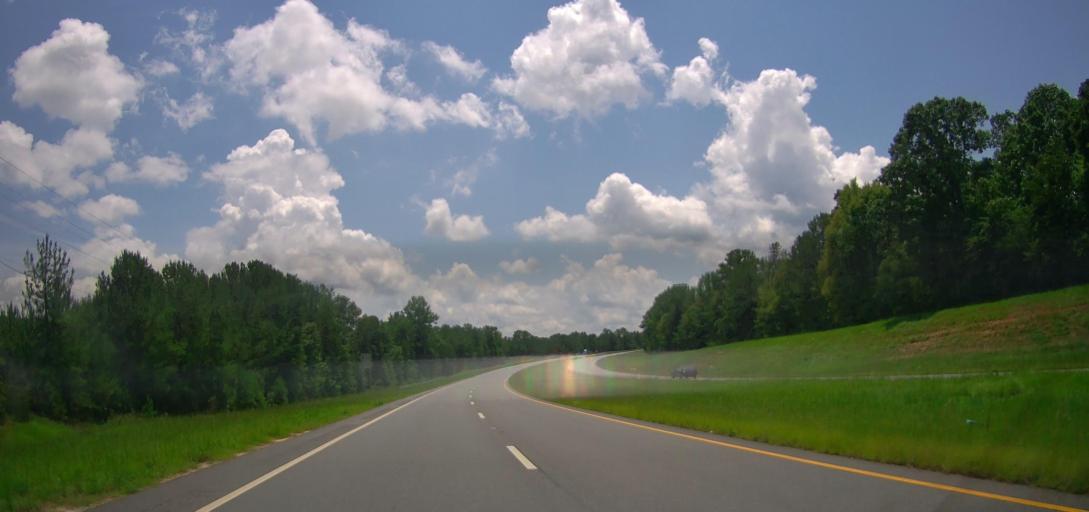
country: US
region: Georgia
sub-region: Upson County
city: Thomaston
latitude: 32.7651
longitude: -84.2449
